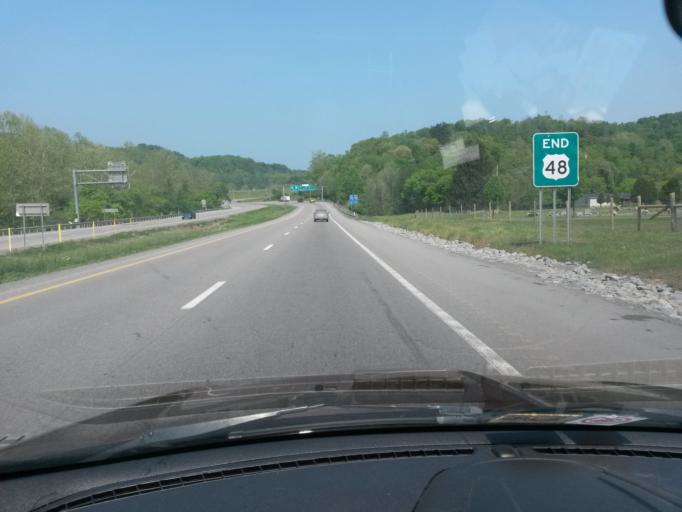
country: US
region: West Virginia
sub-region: Lewis County
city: Weston
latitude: 39.0203
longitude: -80.4206
